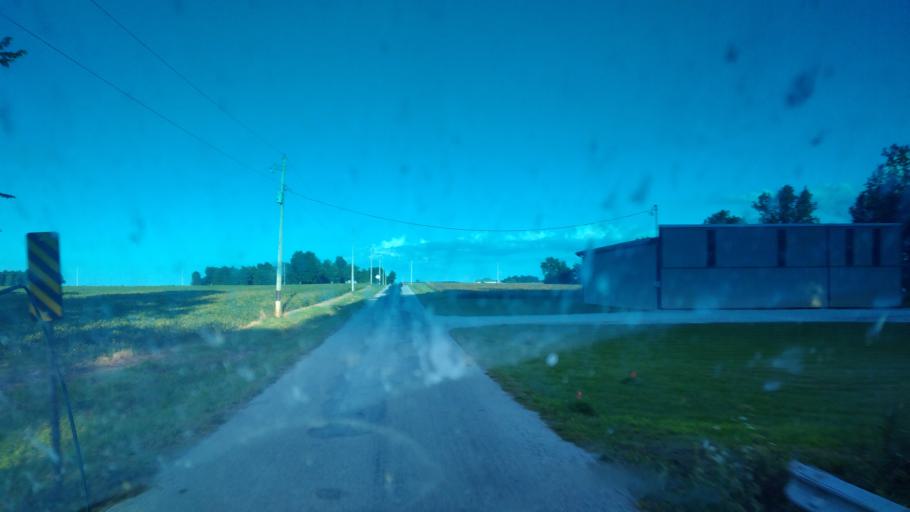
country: US
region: Ohio
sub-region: Wyandot County
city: Upper Sandusky
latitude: 40.8908
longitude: -83.3104
